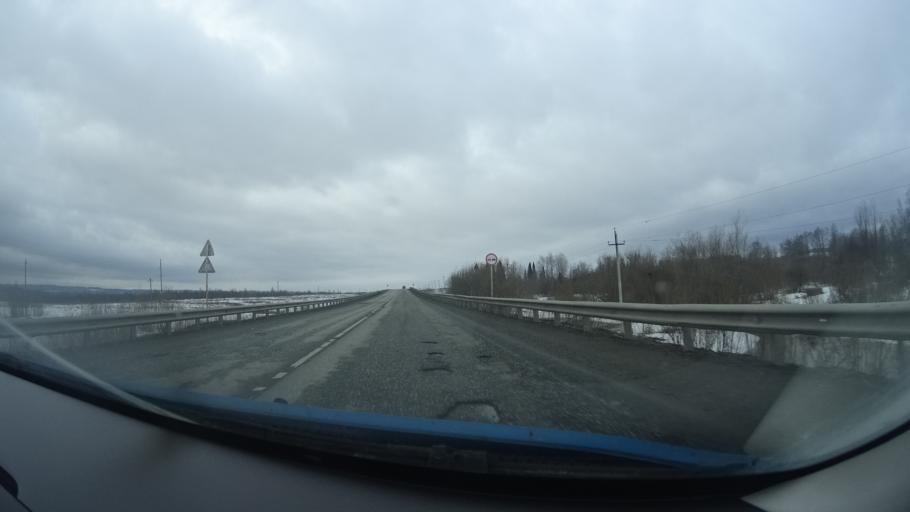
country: RU
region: Perm
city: Barda
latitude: 56.9669
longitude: 55.5786
